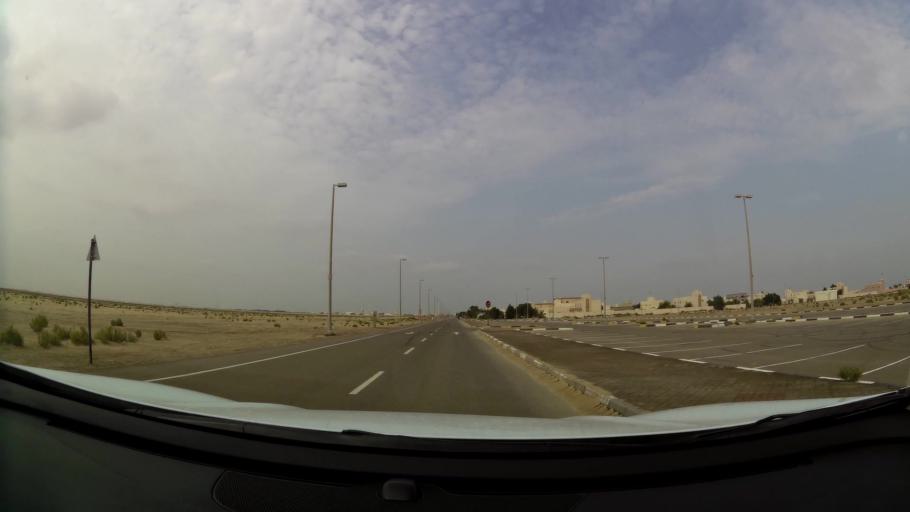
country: AE
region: Abu Dhabi
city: Abu Dhabi
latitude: 24.6324
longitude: 54.6786
